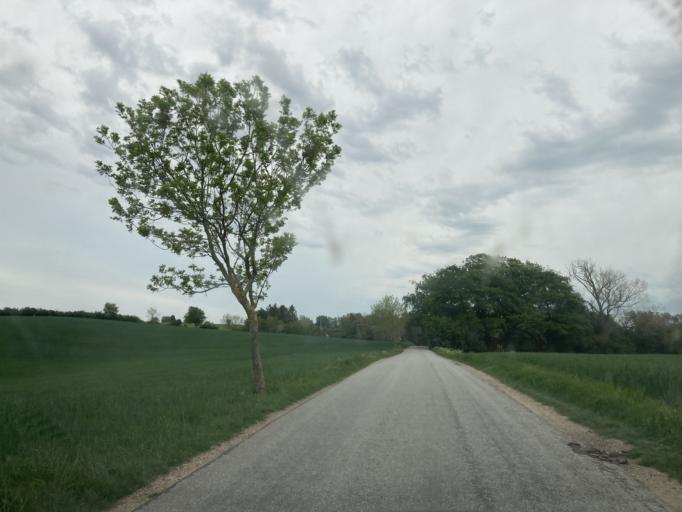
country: DK
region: Zealand
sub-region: Roskilde Kommune
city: Svogerslev
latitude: 55.6749
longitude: 12.0003
